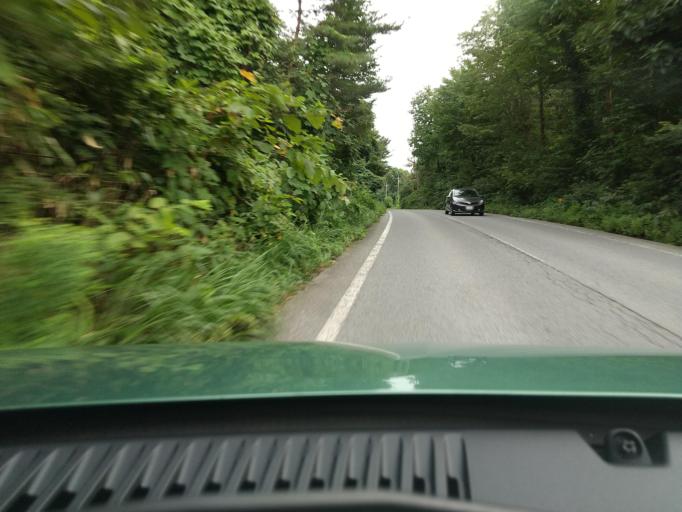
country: JP
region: Akita
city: Akita
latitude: 39.7643
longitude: 140.1328
